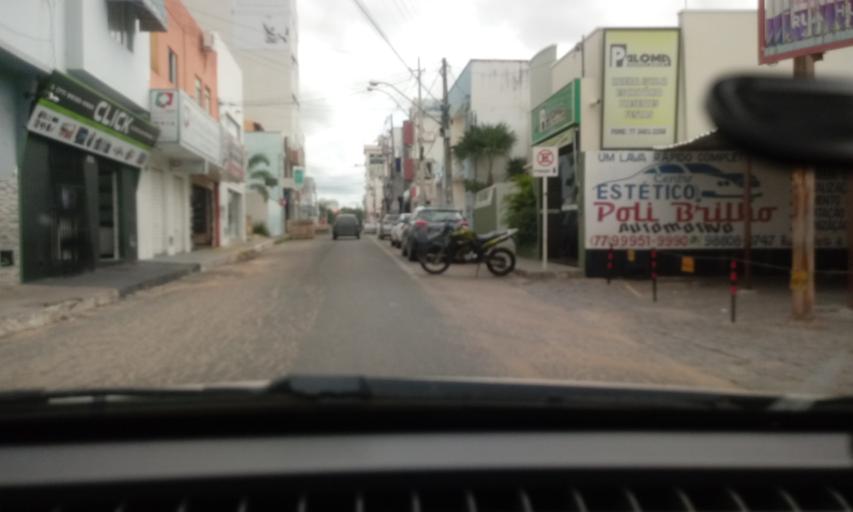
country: BR
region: Bahia
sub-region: Guanambi
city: Guanambi
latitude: -14.2247
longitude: -42.7797
